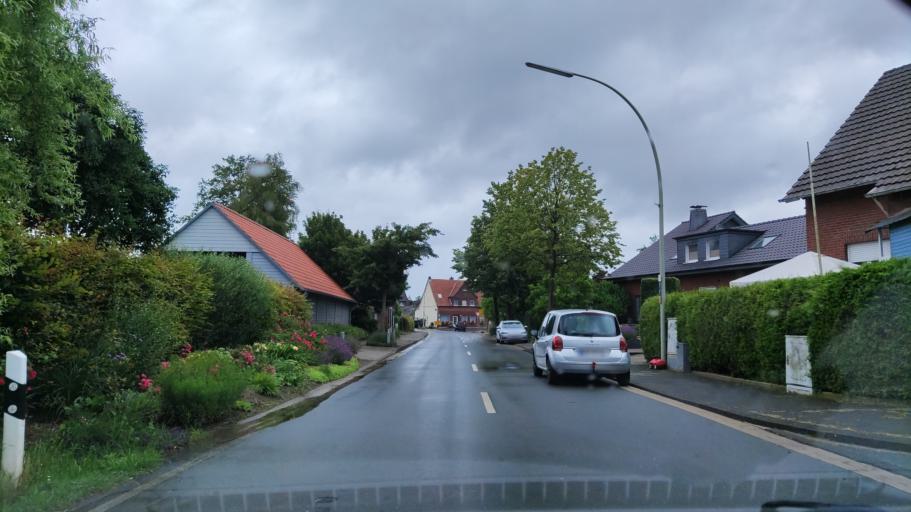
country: DE
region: North Rhine-Westphalia
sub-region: Regierungsbezirk Munster
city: Everswinkel
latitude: 51.9105
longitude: 7.8045
